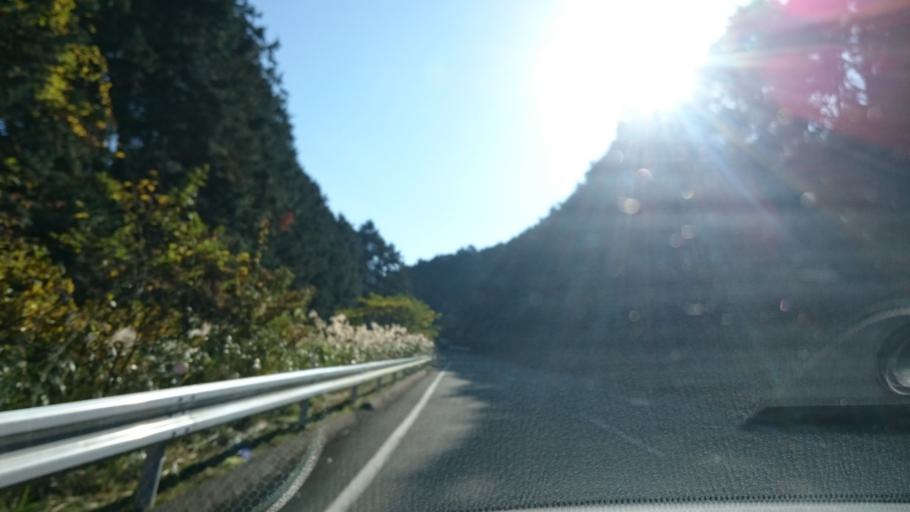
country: JP
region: Shizuoka
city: Heda
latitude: 34.9921
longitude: 138.8115
